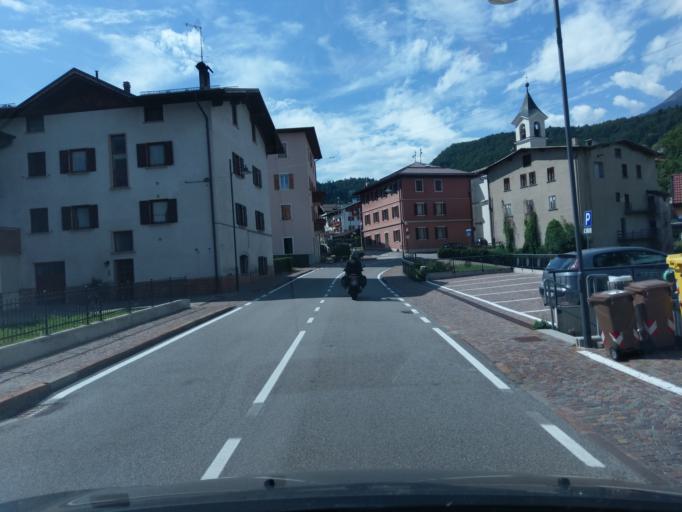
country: IT
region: Trentino-Alto Adige
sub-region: Provincia di Trento
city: Cavedago
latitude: 46.1839
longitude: 11.0288
